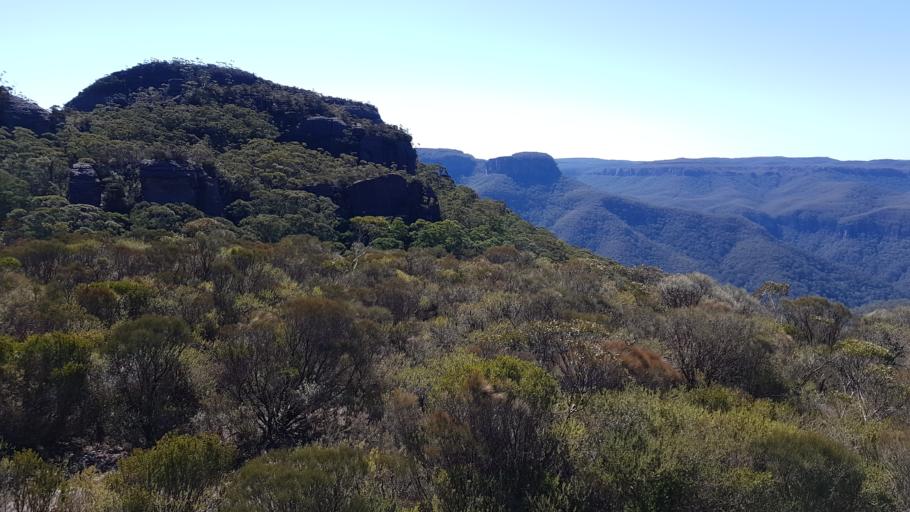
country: AU
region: New South Wales
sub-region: Shoalhaven Shire
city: Milton
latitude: -35.2742
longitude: 150.1880
